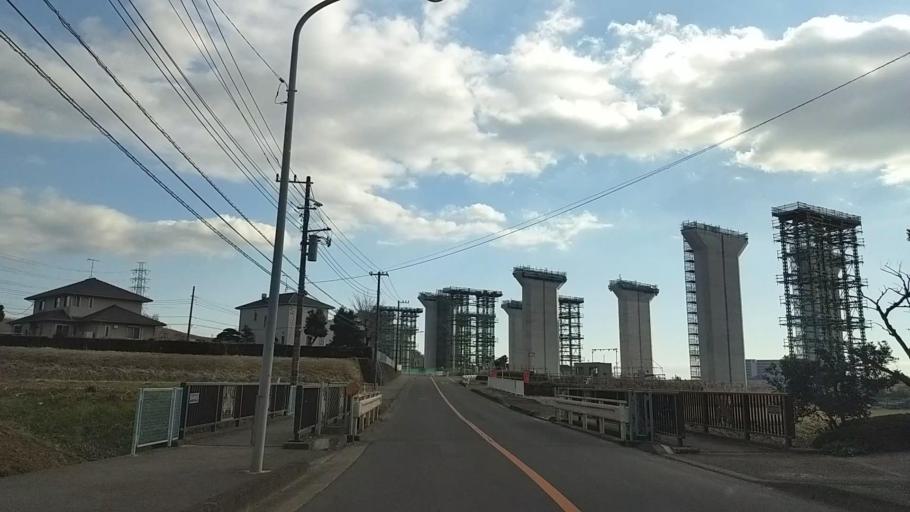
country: JP
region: Kanagawa
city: Isehara
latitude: 35.4166
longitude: 139.3003
